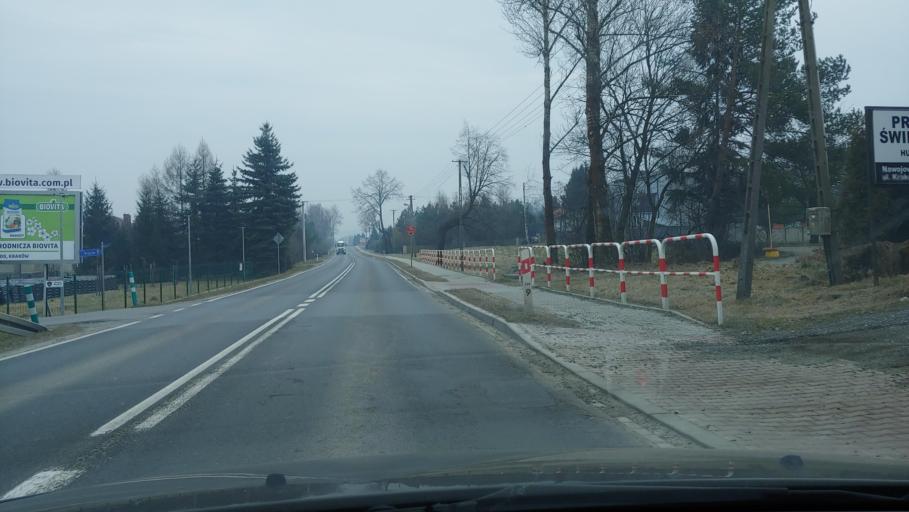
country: PL
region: Lesser Poland Voivodeship
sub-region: Powiat krakowski
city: Krzeszowice
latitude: 50.1272
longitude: 19.6652
